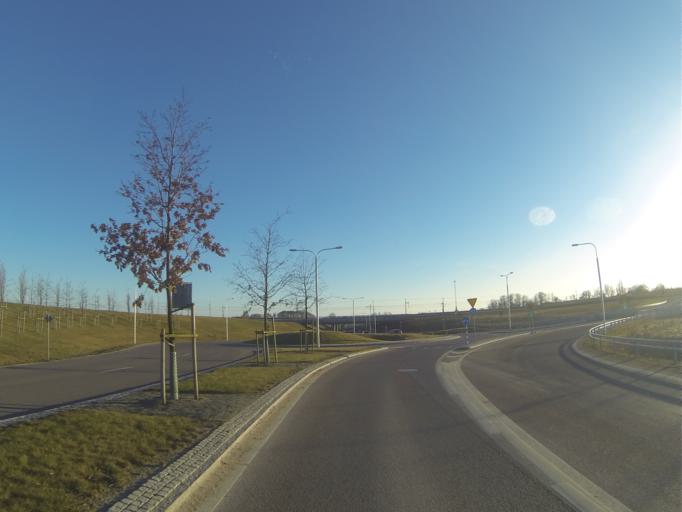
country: SE
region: Skane
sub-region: Malmo
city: Bunkeflostrand
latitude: 55.5488
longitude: 12.9823
